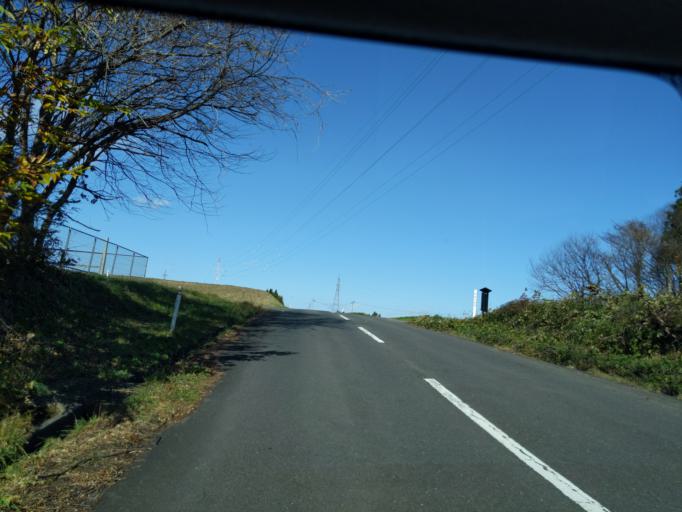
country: JP
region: Iwate
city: Mizusawa
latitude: 39.0853
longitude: 141.1249
